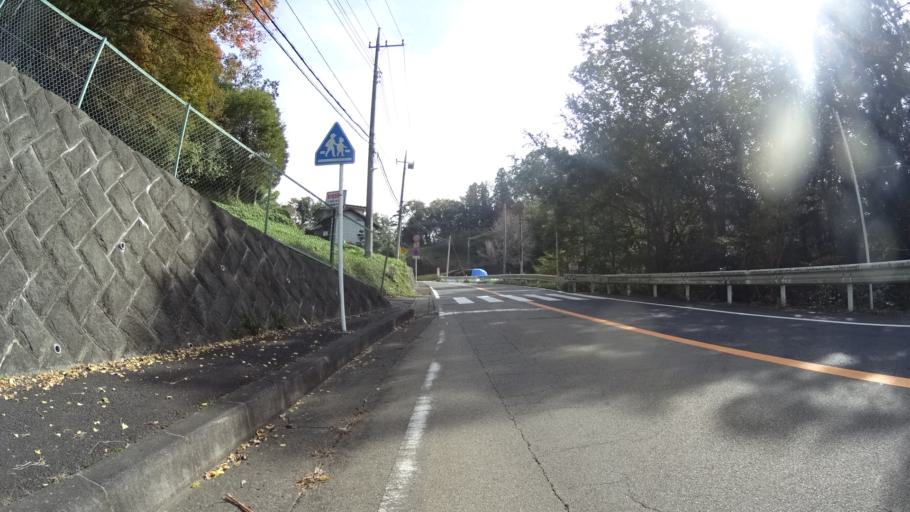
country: JP
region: Yamanashi
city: Uenohara
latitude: 35.5835
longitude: 139.1406
